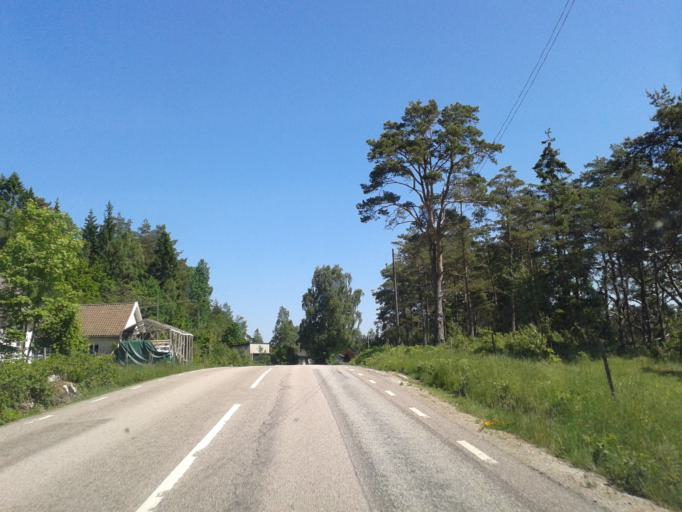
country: SE
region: Vaestra Goetaland
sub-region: Orust
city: Henan
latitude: 58.2426
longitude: 11.7152
